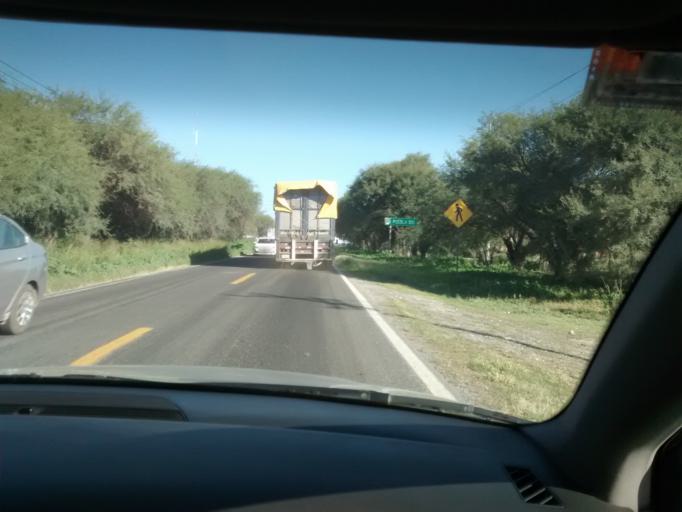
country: MX
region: Puebla
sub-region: Tepanco de Lopez
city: San Andres Cacaloapan
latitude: 18.5506
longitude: -97.5518
